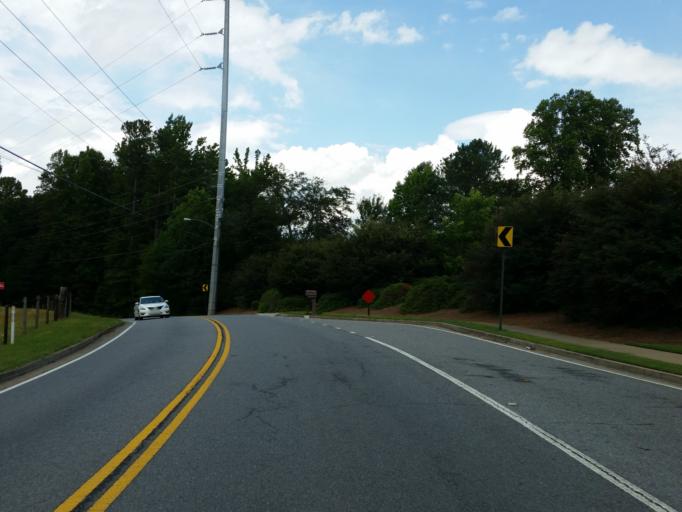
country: US
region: Georgia
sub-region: Fulton County
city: Roswell
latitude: 34.0343
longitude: -84.4277
